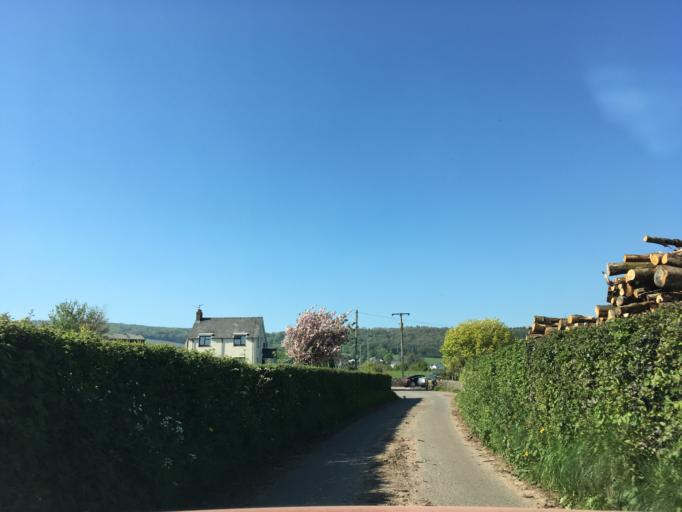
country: GB
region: Wales
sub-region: Newport
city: Llanvaches
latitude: 51.6194
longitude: -2.7962
